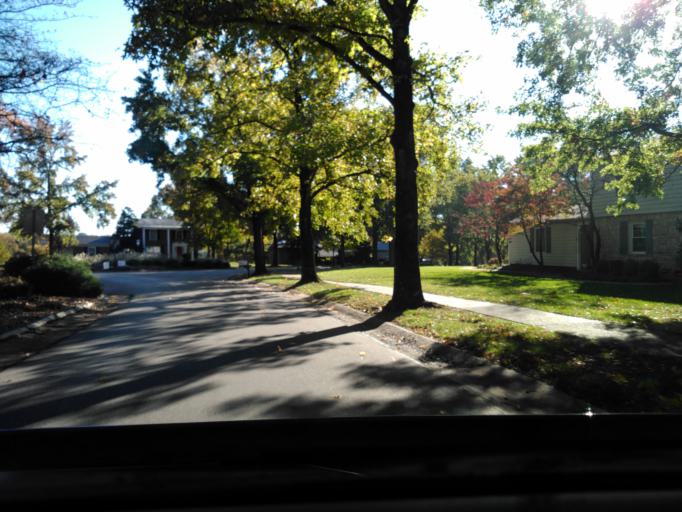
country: US
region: Missouri
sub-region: Saint Louis County
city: Town and Country
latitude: 38.6120
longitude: -90.4834
